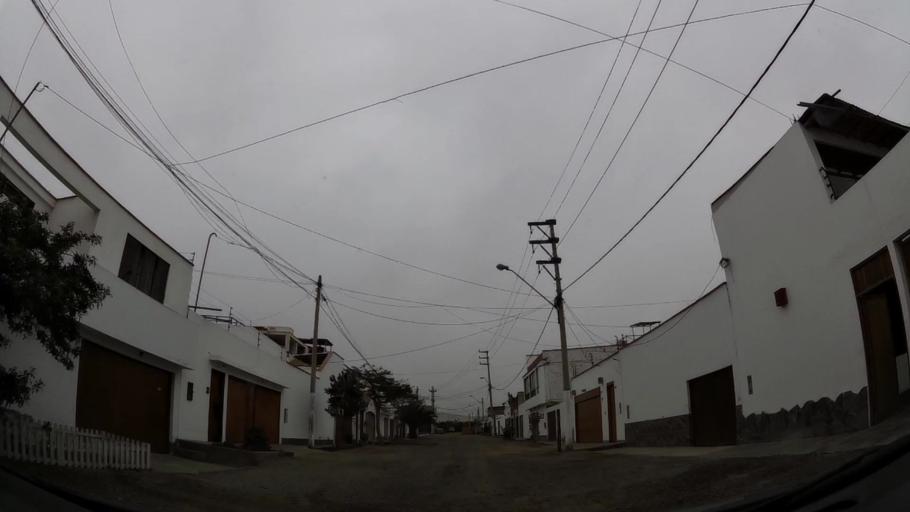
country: PE
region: Lima
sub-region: Lima
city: Punta Hermosa
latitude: -12.3298
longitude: -76.8289
